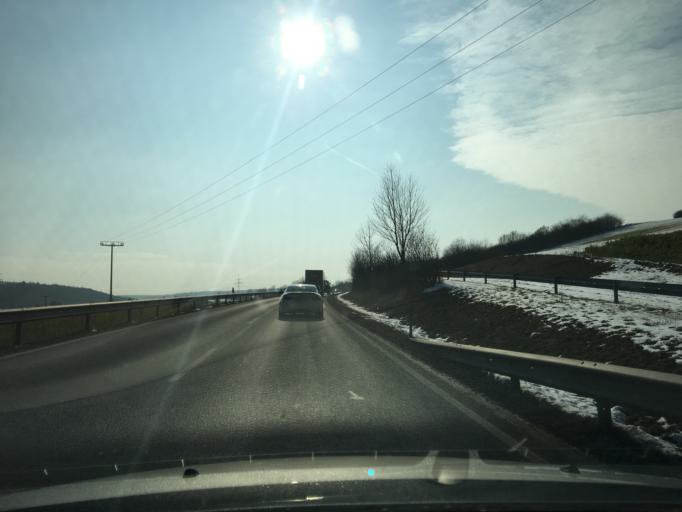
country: DE
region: Bavaria
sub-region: Lower Bavaria
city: Gottfrieding
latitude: 48.6258
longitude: 12.5258
